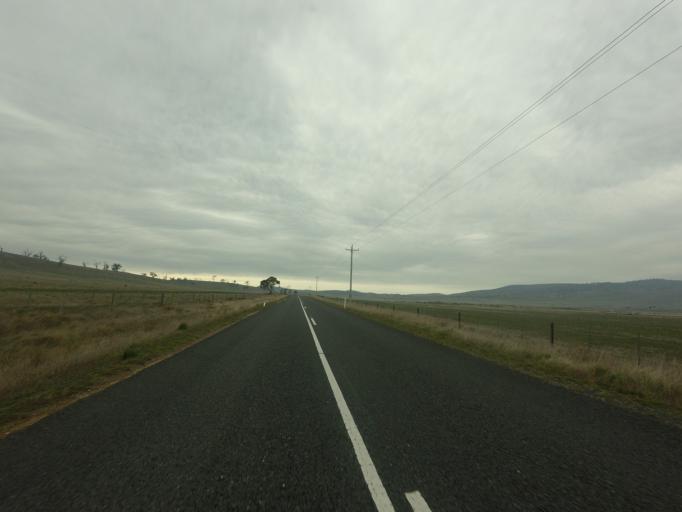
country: AU
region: Tasmania
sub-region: Derwent Valley
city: New Norfolk
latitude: -42.4405
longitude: 146.9778
